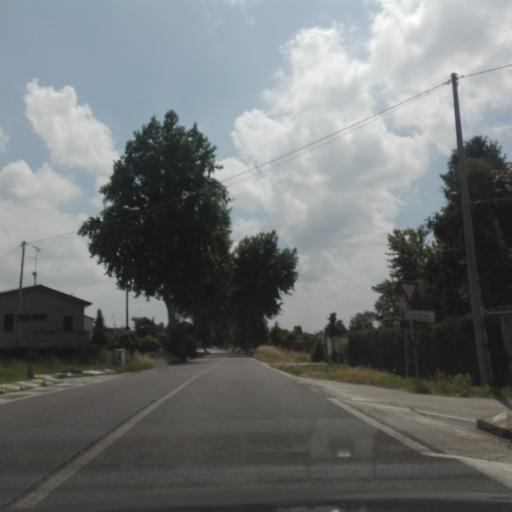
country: IT
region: Veneto
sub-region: Provincia di Rovigo
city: Villadose
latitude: 45.0676
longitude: 11.8929
